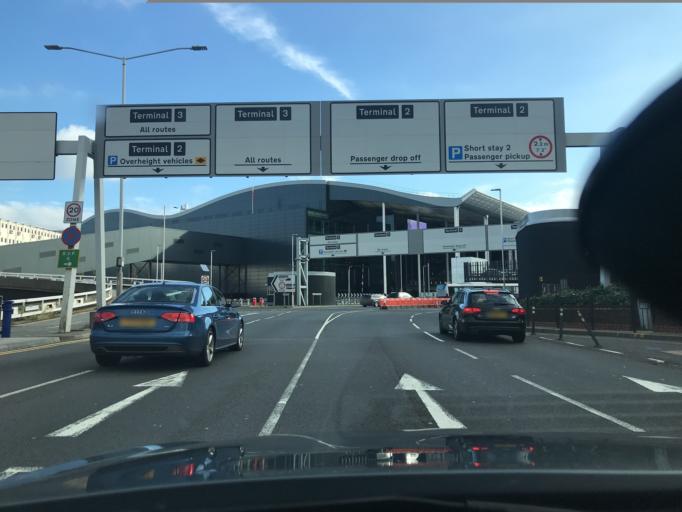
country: GB
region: England
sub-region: Greater London
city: West Drayton
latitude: 51.4716
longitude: -0.4523
